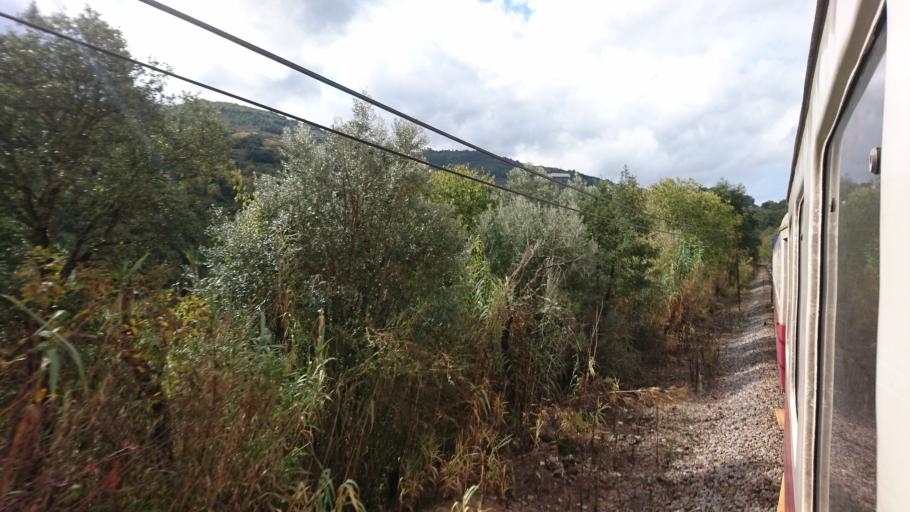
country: PT
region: Viseu
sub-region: Resende
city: Resende
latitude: 41.1213
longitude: -7.9190
